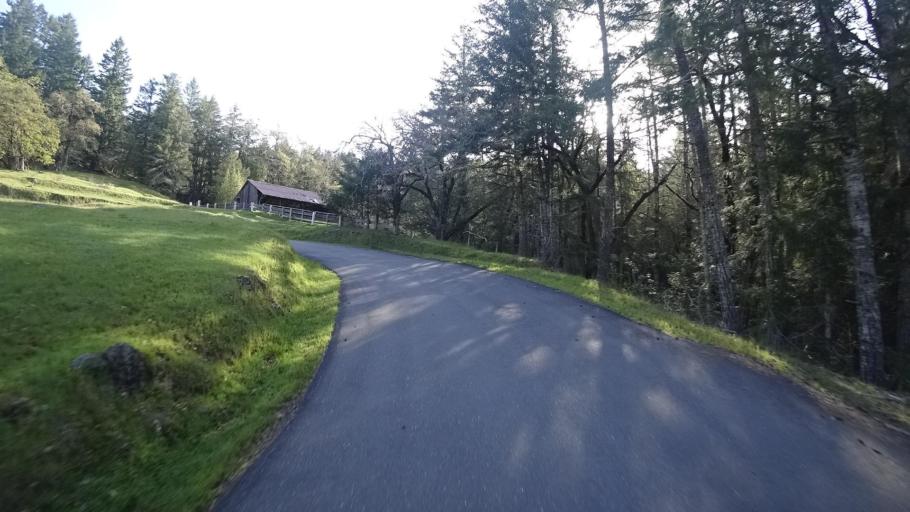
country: US
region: California
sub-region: Humboldt County
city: Blue Lake
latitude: 40.7087
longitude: -123.9364
